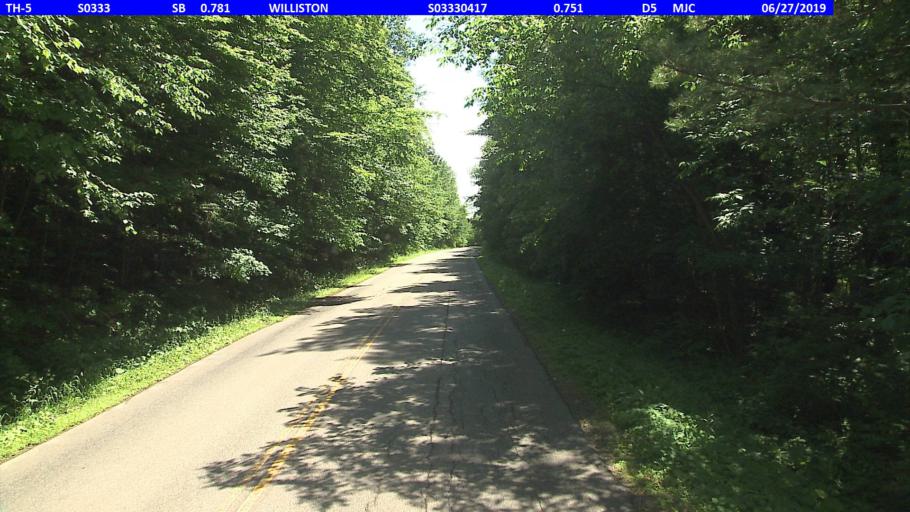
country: US
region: Vermont
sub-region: Chittenden County
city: South Burlington
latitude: 44.4122
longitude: -73.1392
